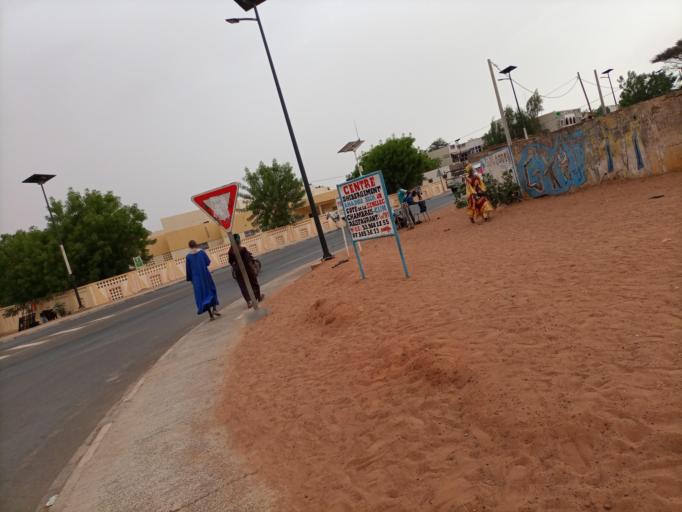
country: SN
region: Louga
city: Ndibene Dahra
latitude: 15.3954
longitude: -15.1144
